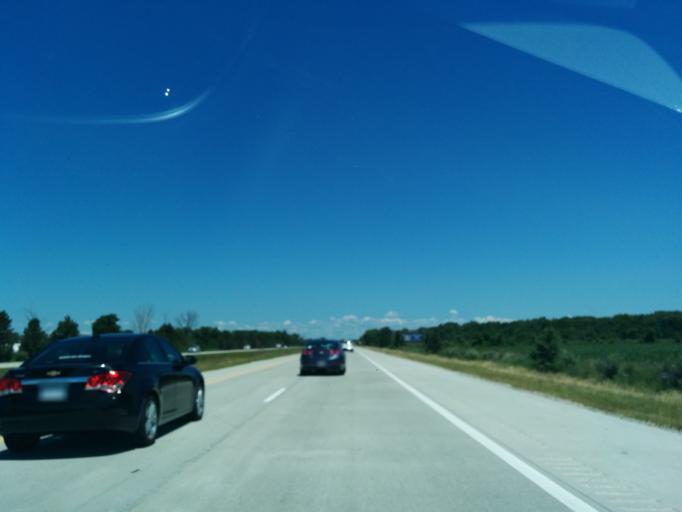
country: US
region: Michigan
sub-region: Bay County
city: Pinconning
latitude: 43.9012
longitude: -84.0199
